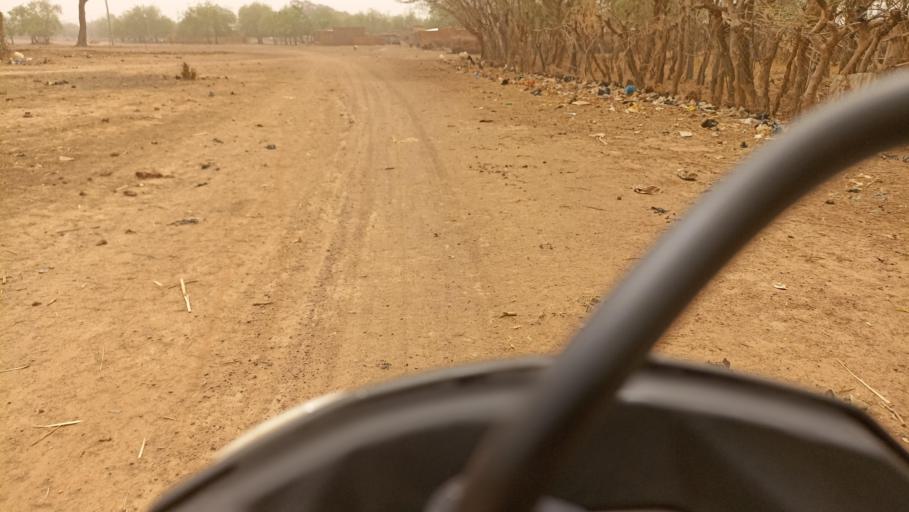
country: BF
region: Nord
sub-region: Province du Zondoma
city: Gourcy
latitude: 13.2480
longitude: -2.5893
